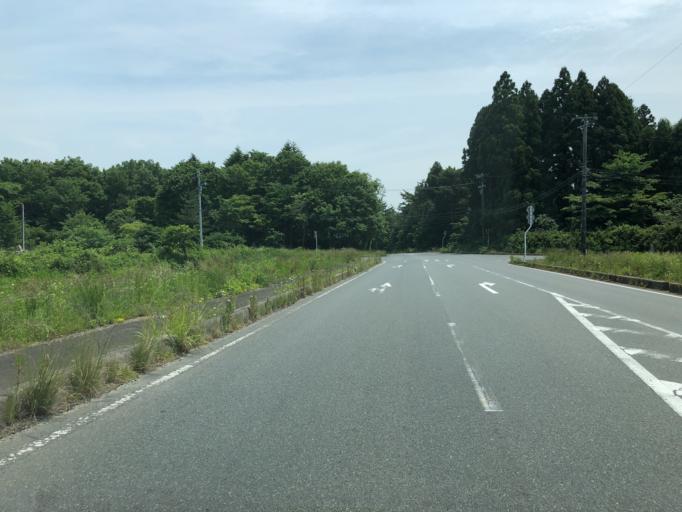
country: JP
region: Fukushima
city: Namie
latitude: 37.5910
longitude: 140.9339
